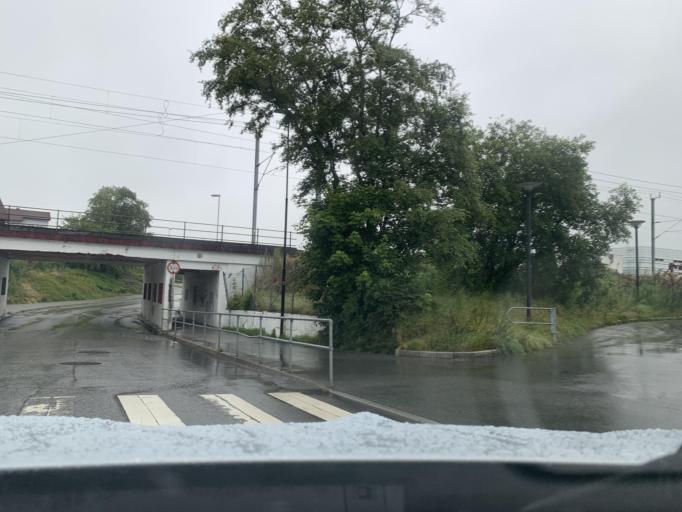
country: NO
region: Rogaland
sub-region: Time
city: Bryne
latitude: 58.7307
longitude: 5.6491
